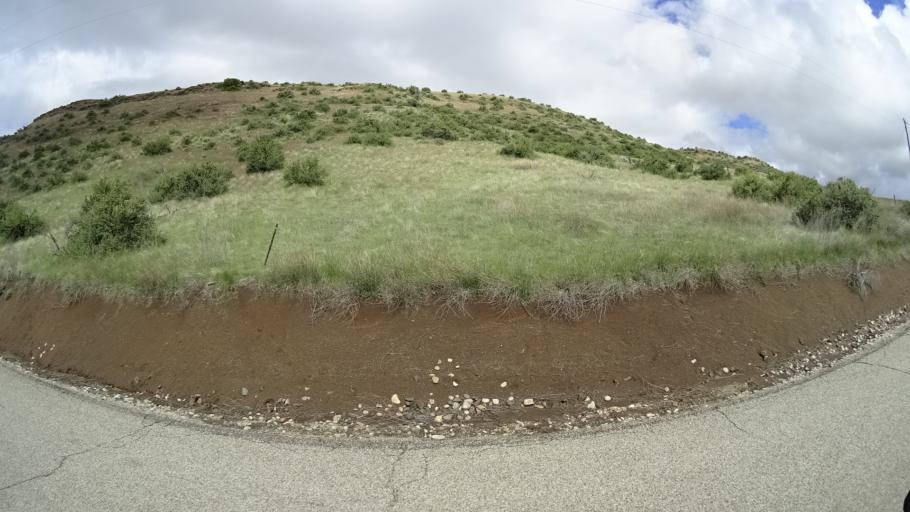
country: US
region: Idaho
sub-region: Ada County
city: Garden City
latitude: 43.7342
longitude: -116.2290
